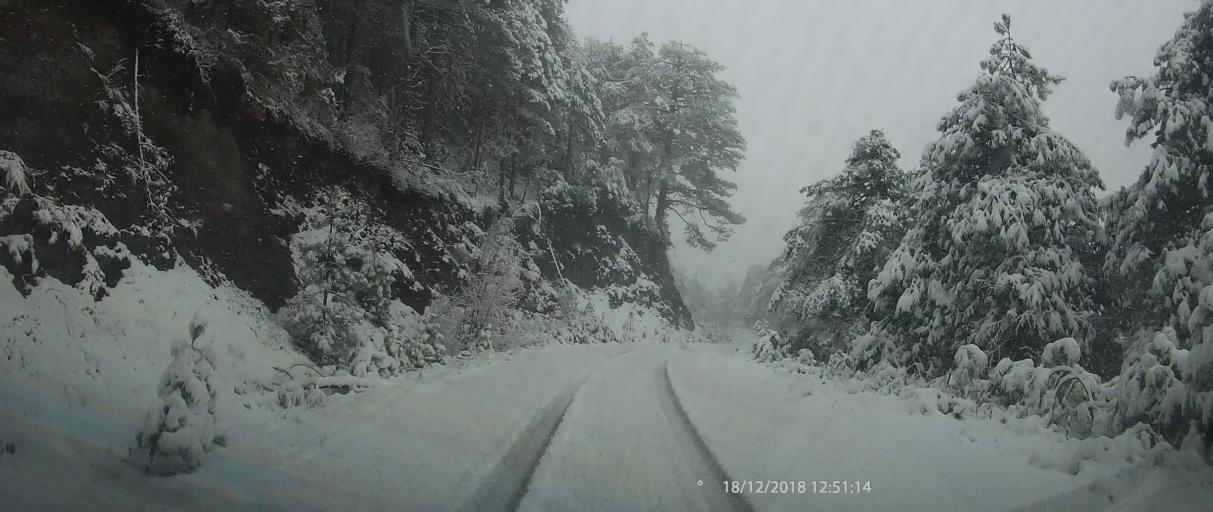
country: GR
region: Central Macedonia
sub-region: Nomos Pierias
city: Litochoro
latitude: 40.1034
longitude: 22.4474
